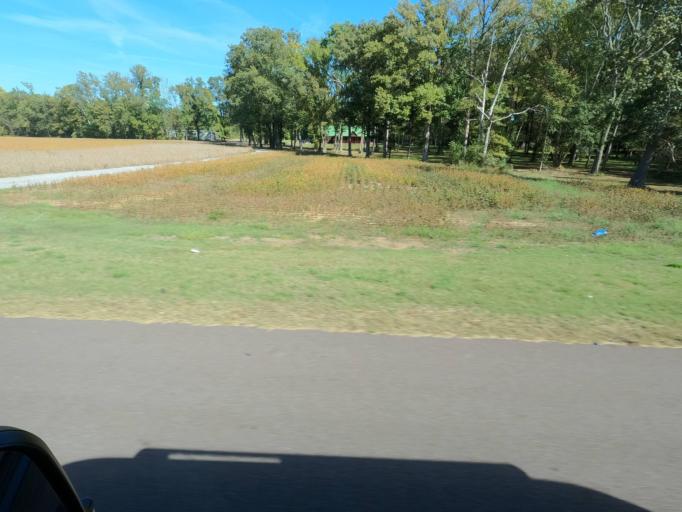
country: US
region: Tennessee
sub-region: Lauderdale County
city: Halls
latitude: 35.9254
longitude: -89.2809
